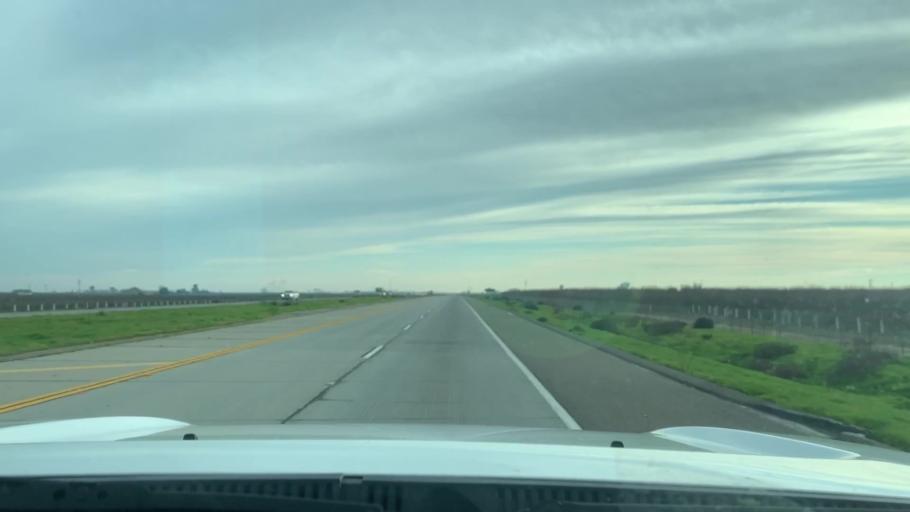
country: US
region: California
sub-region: Fresno County
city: Caruthers
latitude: 36.5809
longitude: -119.7862
